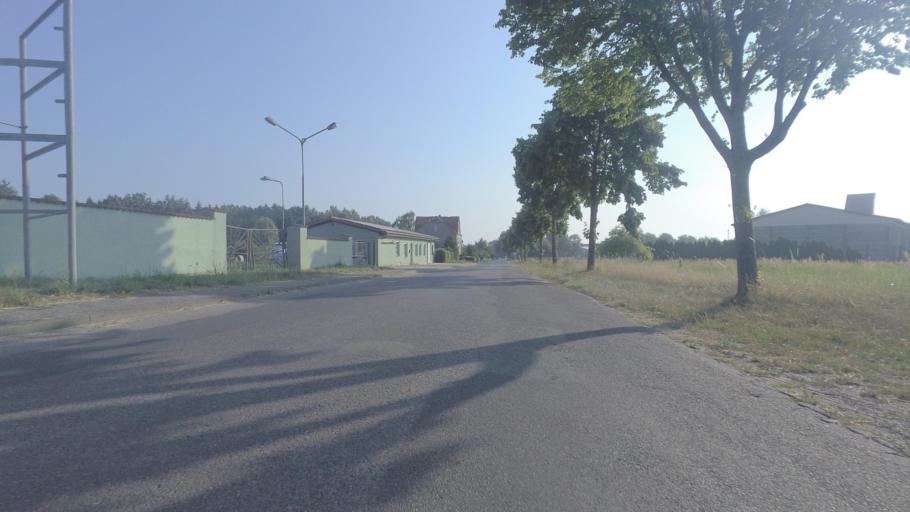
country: DE
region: Brandenburg
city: Heiligengrabe
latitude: 53.2790
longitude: 12.3455
